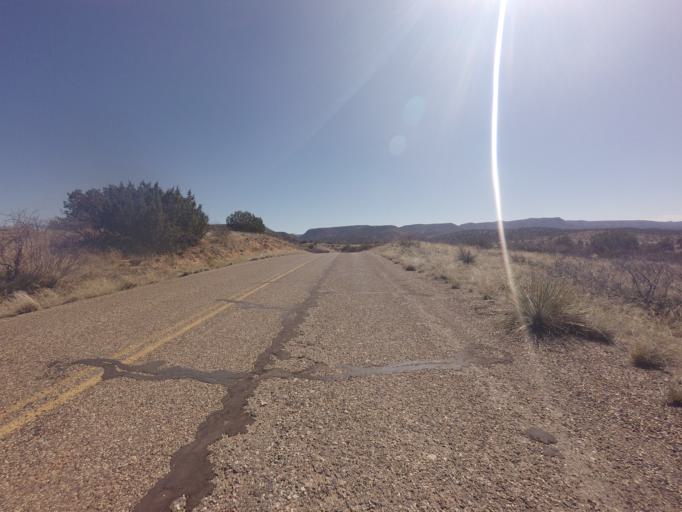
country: US
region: Arizona
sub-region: Yavapai County
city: Lake Montezuma
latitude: 34.6837
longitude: -111.7336
